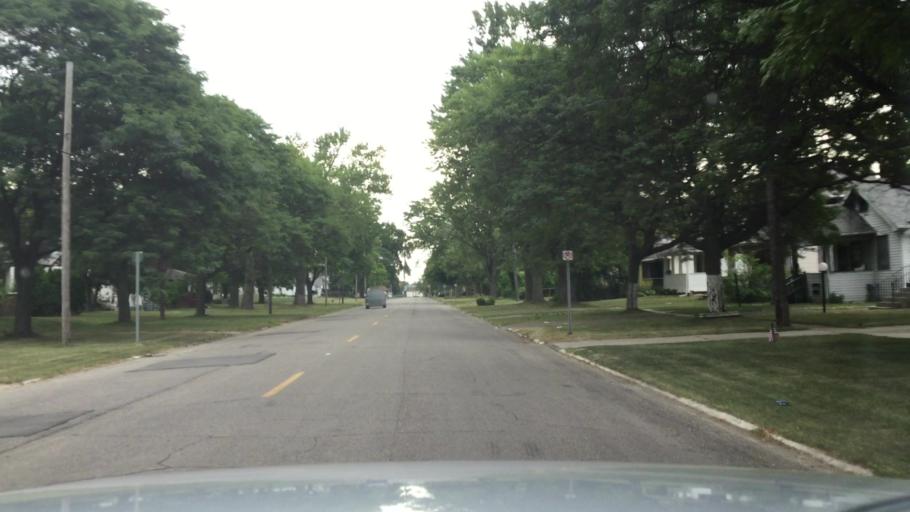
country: US
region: Michigan
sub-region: Genesee County
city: Beecher
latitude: 43.0560
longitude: -83.6986
